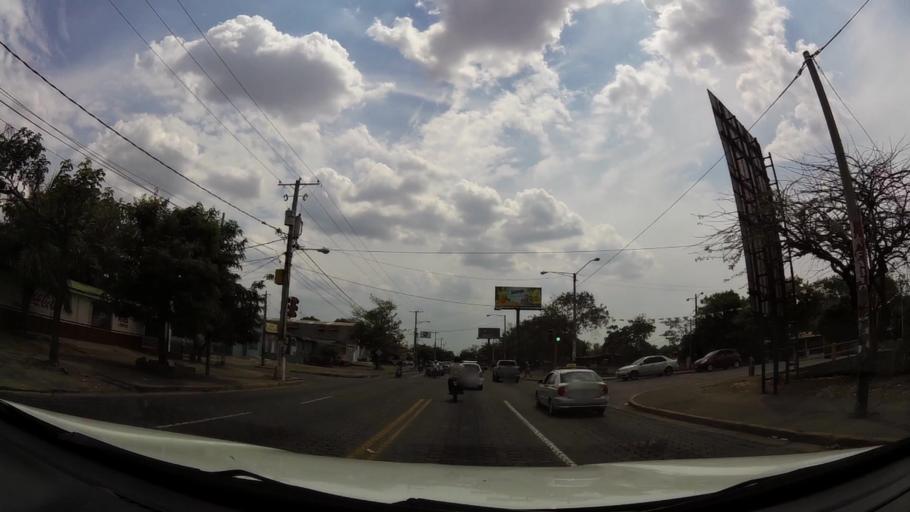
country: NI
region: Managua
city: Managua
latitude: 12.1393
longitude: -86.2466
